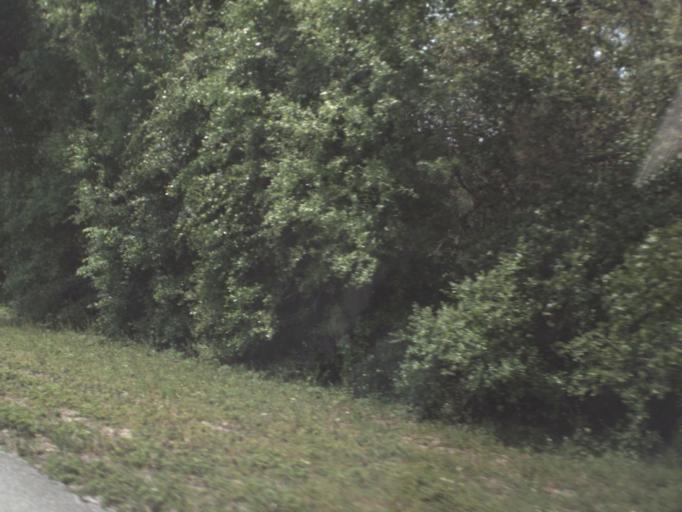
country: US
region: Florida
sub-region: Lake County
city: Astor
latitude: 29.2897
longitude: -81.6549
